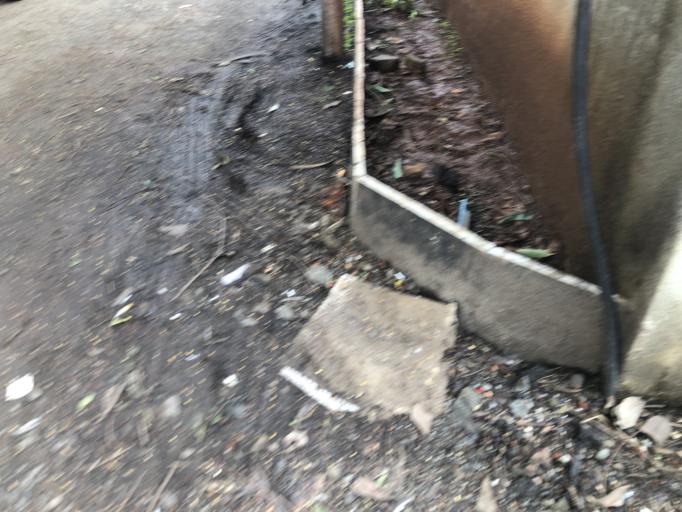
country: IN
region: Maharashtra
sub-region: Pune Division
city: Pimpri
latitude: 18.5915
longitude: 73.7851
